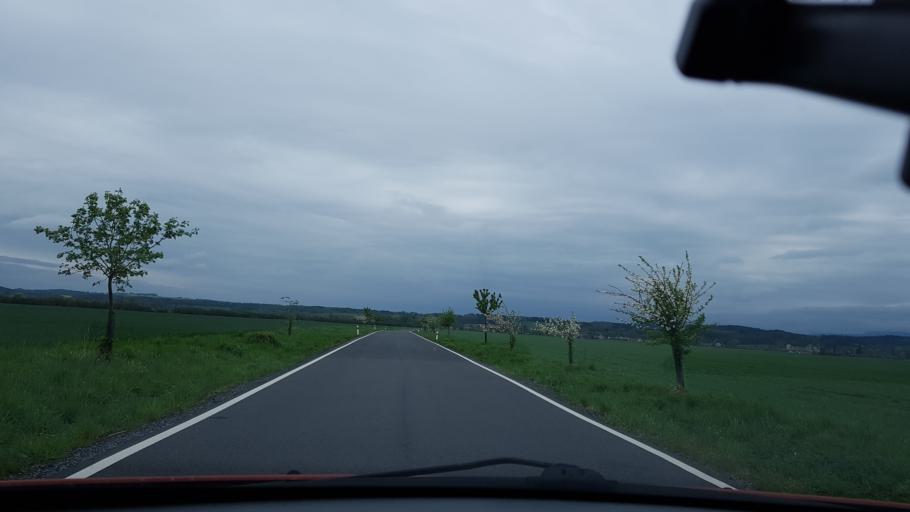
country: CZ
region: Olomoucky
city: Vidnava
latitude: 50.3799
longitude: 17.1578
